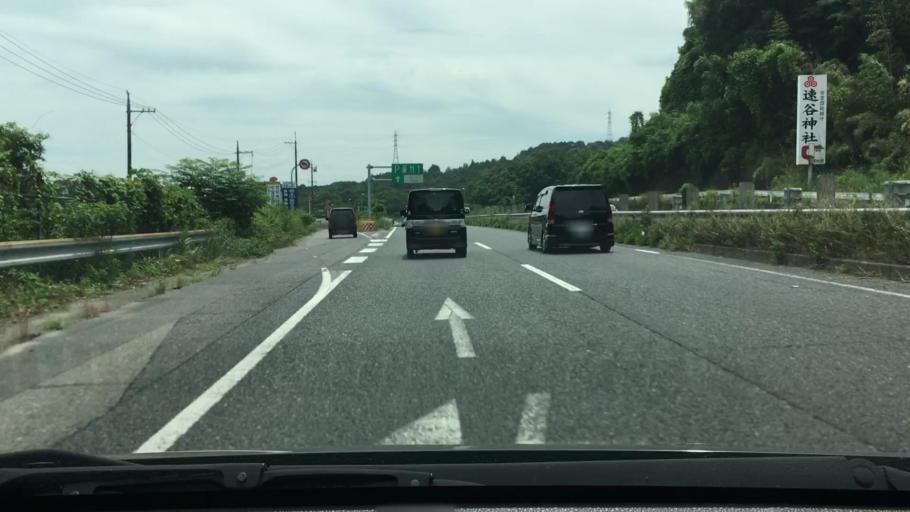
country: JP
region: Hiroshima
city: Hatsukaichi
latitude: 34.3702
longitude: 132.3345
